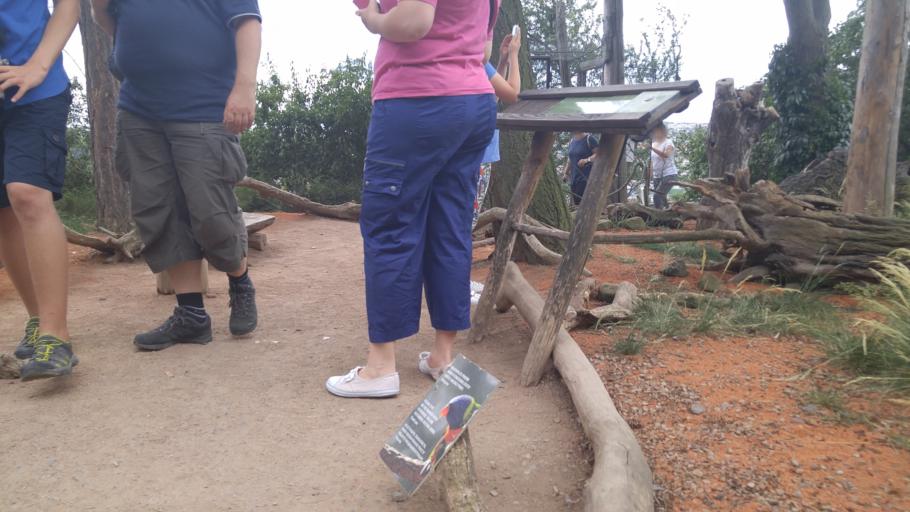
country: CZ
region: Praha
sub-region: Praha 1
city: Mala Strana
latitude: 50.1175
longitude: 14.4061
